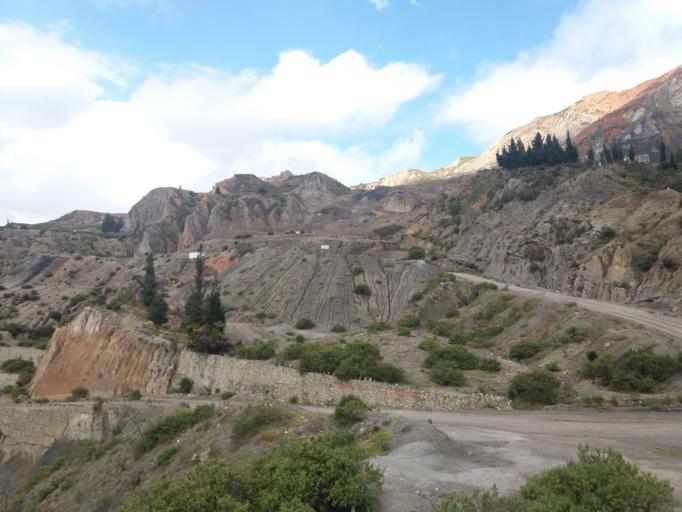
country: BO
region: La Paz
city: La Paz
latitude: -16.5524
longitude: -68.0707
